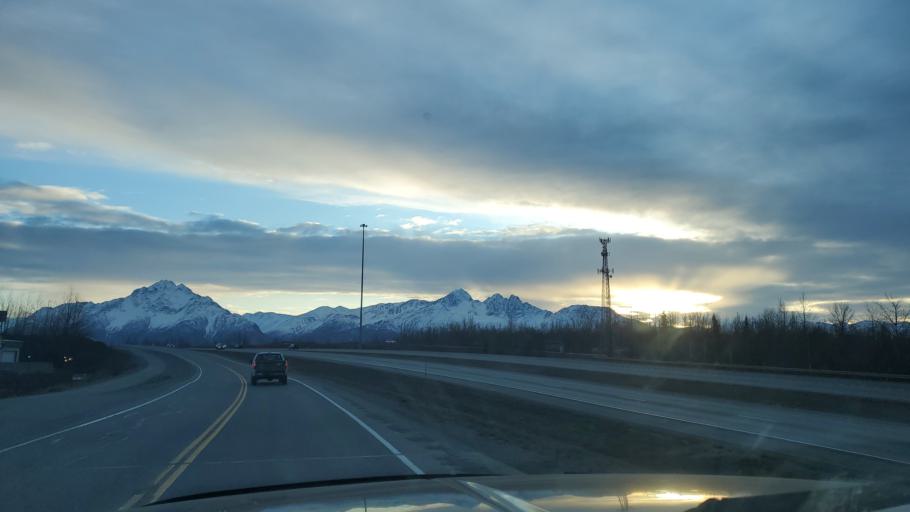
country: US
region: Alaska
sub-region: Matanuska-Susitna Borough
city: Lakes
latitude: 61.5651
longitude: -149.3056
